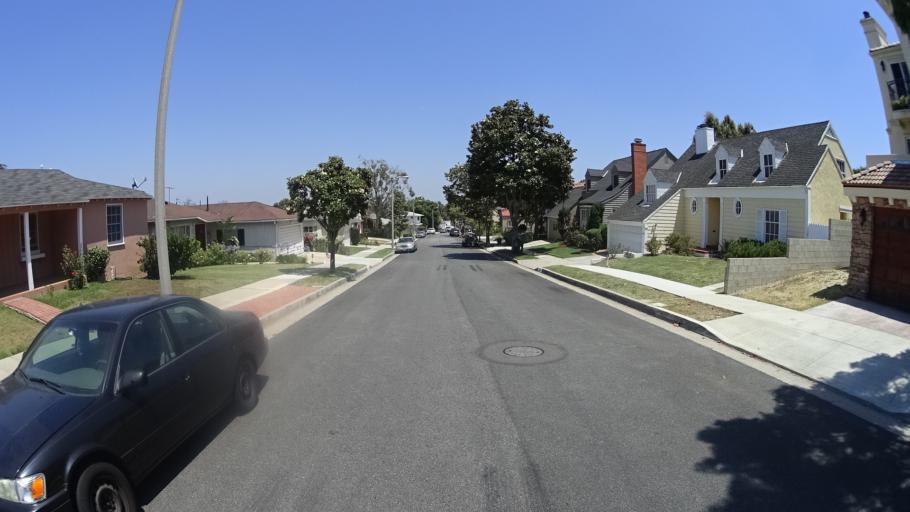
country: US
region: California
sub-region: Los Angeles County
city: View Park-Windsor Hills
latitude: 34.0005
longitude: -118.3406
